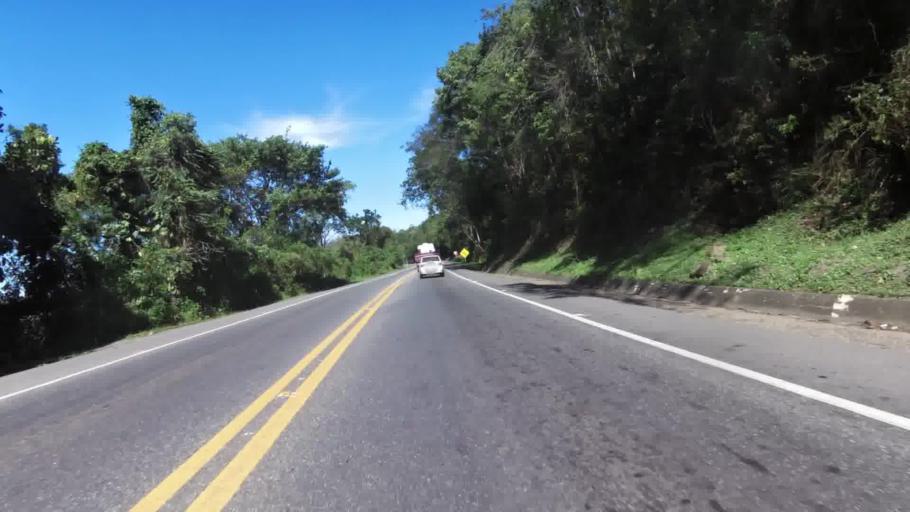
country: BR
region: Espirito Santo
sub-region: Iconha
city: Iconha
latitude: -20.8104
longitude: -40.8373
